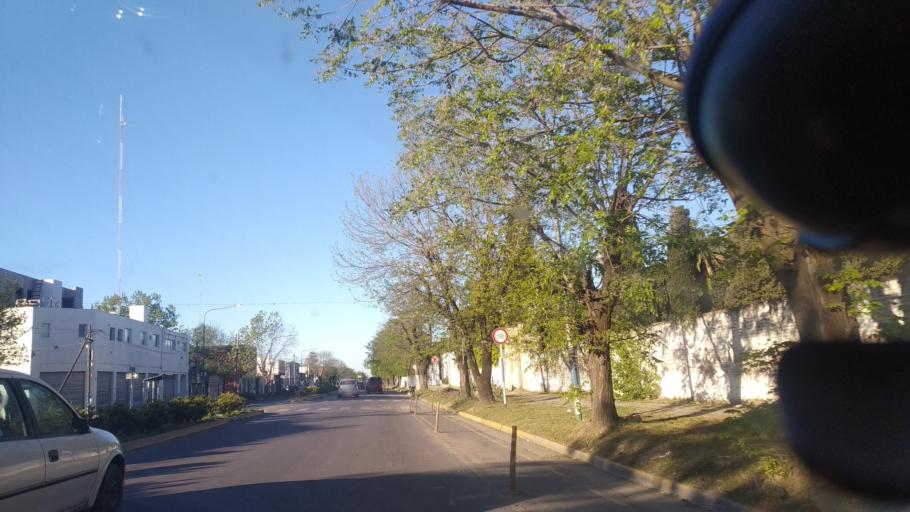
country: AR
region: Buenos Aires
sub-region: Partido de La Plata
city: La Plata
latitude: -34.9581
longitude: -57.9575
